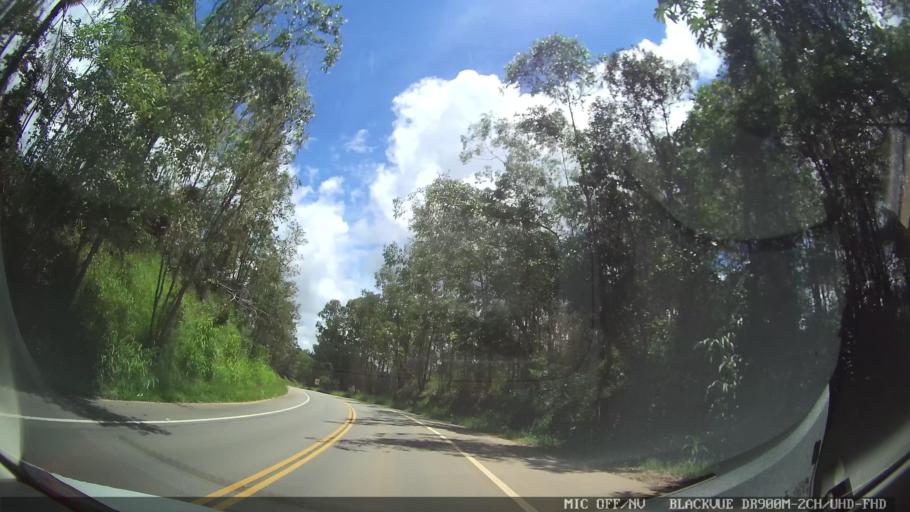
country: BR
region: Sao Paulo
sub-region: Amparo
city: Amparo
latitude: -22.7808
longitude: -46.7167
